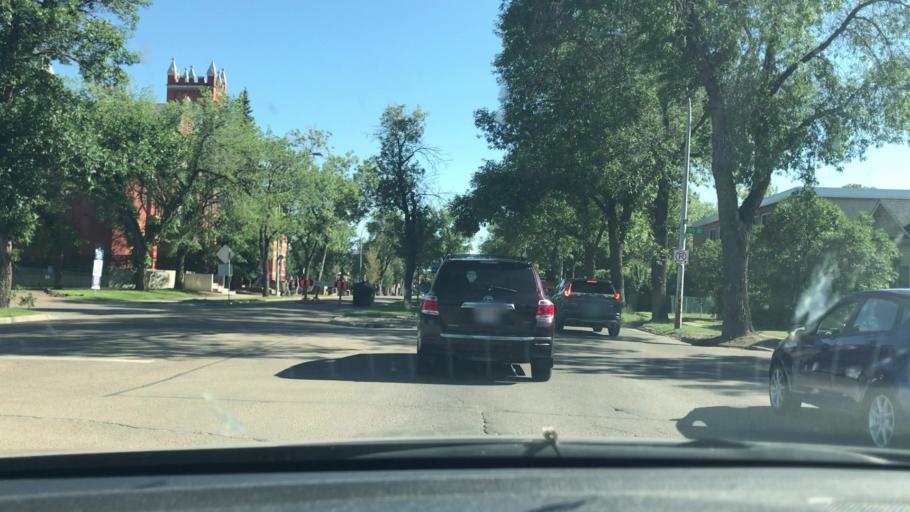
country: CA
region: Alberta
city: Edmonton
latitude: 53.5209
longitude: -113.4976
